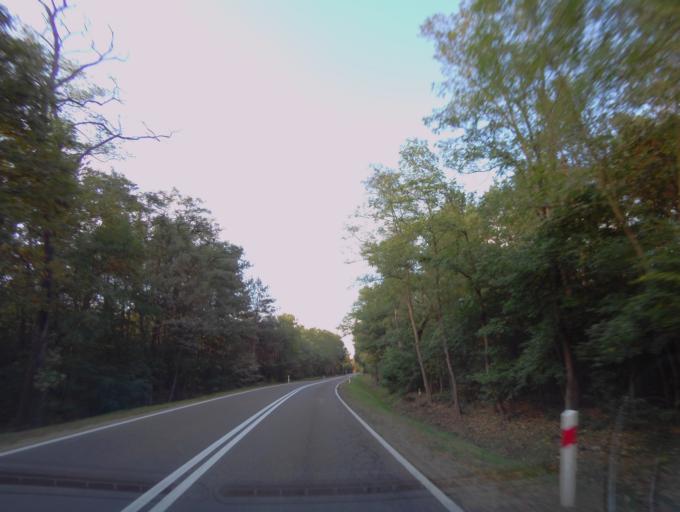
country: PL
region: Subcarpathian Voivodeship
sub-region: Powiat nizanski
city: Krzeszow
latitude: 50.3746
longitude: 22.3126
